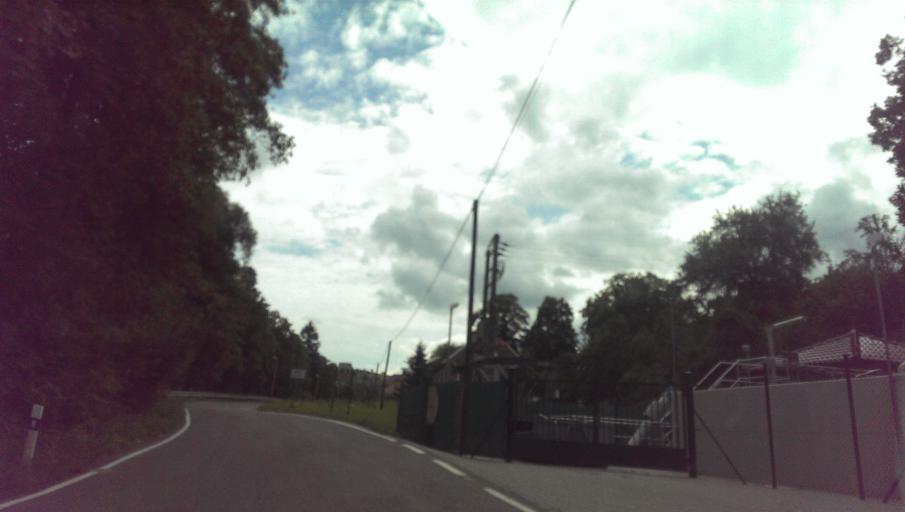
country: CZ
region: South Moravian
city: Velka nad Velickou
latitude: 48.8681
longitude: 17.5887
